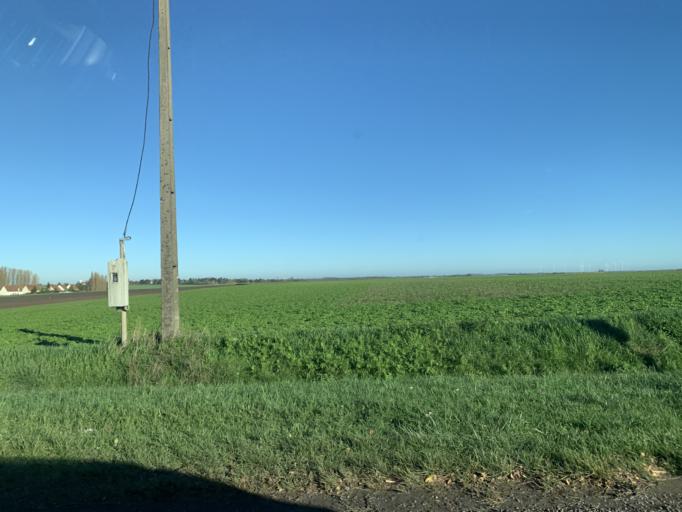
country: FR
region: Nord-Pas-de-Calais
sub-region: Departement du Nord
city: Escaudoeuvres
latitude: 50.1656
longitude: 3.2748
